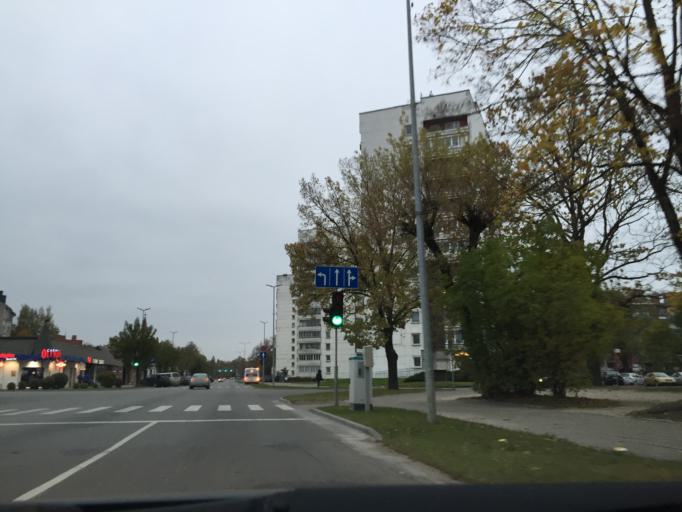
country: LV
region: Jelgava
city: Jelgava
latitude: 56.6472
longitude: 23.7256
